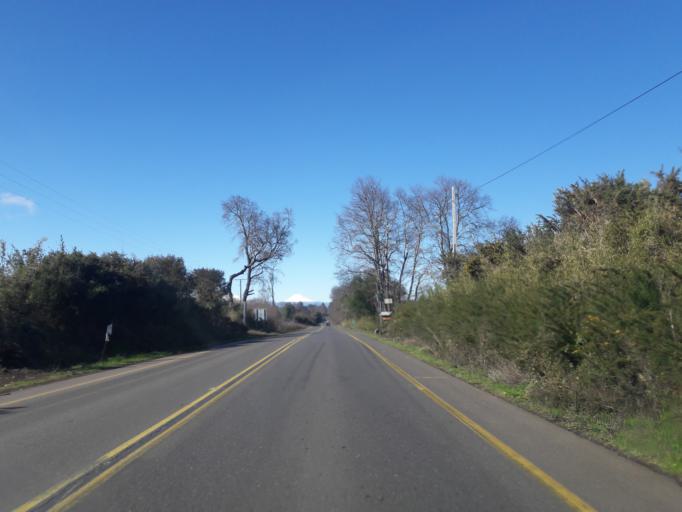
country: CL
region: Araucania
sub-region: Provincia de Malleco
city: Victoria
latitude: -38.2612
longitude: -72.2484
